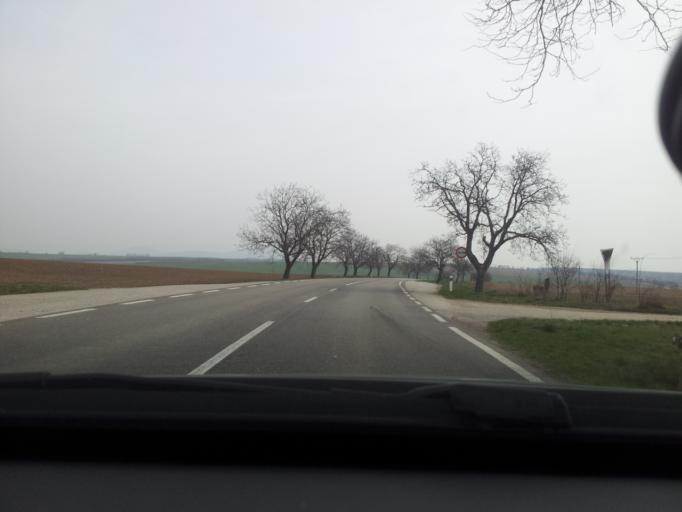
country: SK
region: Nitriansky
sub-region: Okres Nitra
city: Nitra
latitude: 48.3535
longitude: 17.9460
